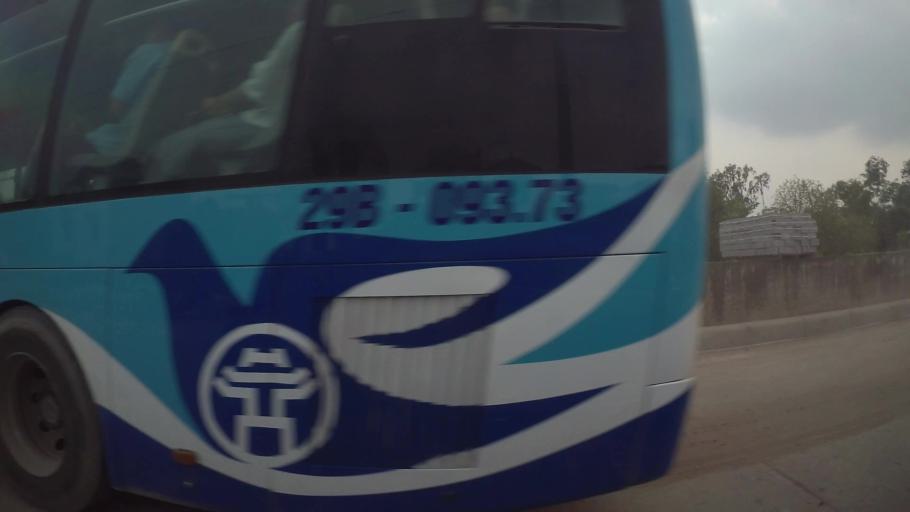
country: VN
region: Ha Noi
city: Trau Quy
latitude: 21.0211
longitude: 105.9003
